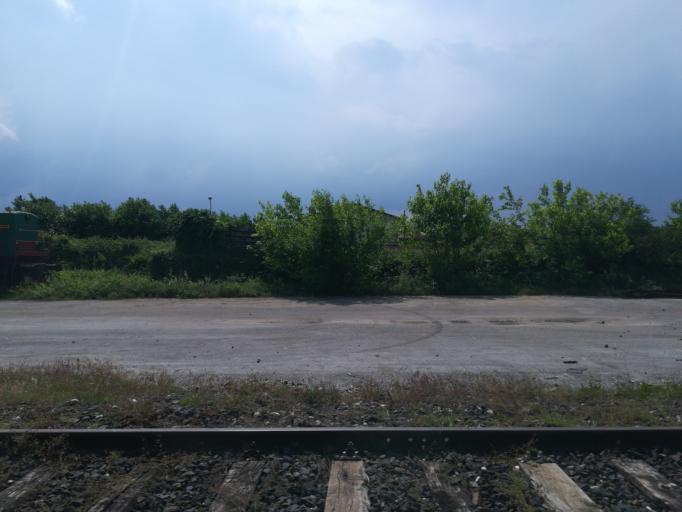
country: IT
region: Veneto
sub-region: Provincia di Vicenza
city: Dueville
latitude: 45.6355
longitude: 11.5455
